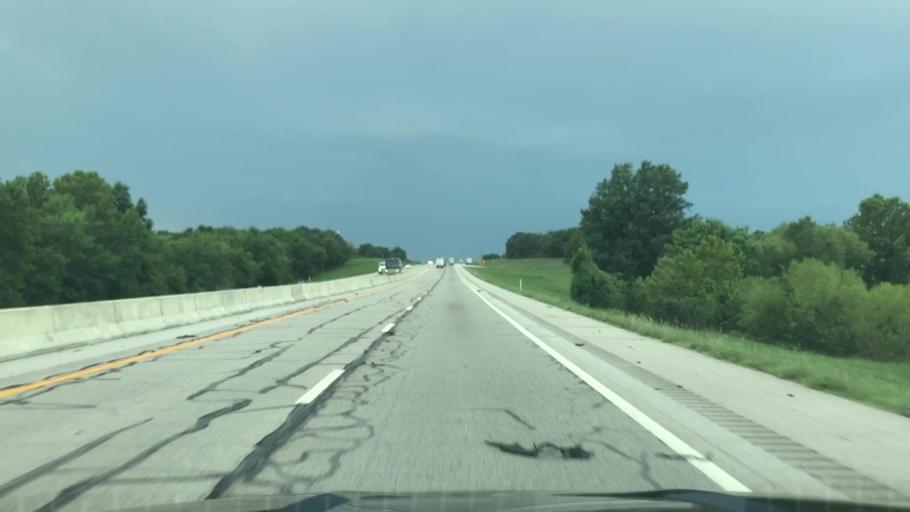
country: US
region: Oklahoma
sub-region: Rogers County
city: Chelsea
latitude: 36.4371
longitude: -95.3822
